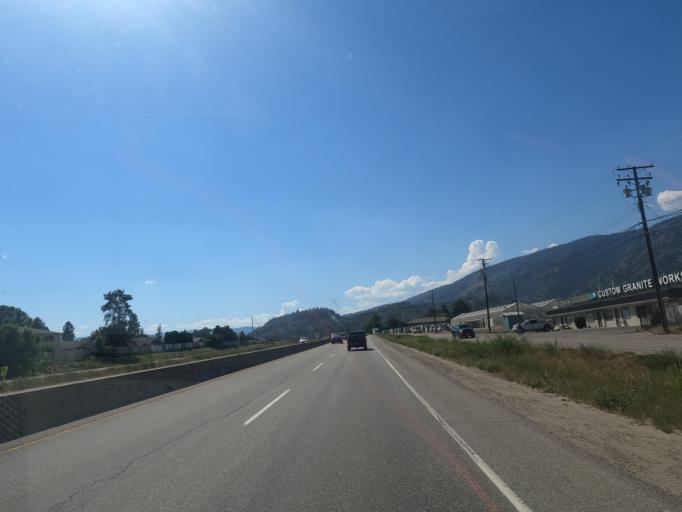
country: CA
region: British Columbia
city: West Kelowna
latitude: 49.8627
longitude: -119.5795
